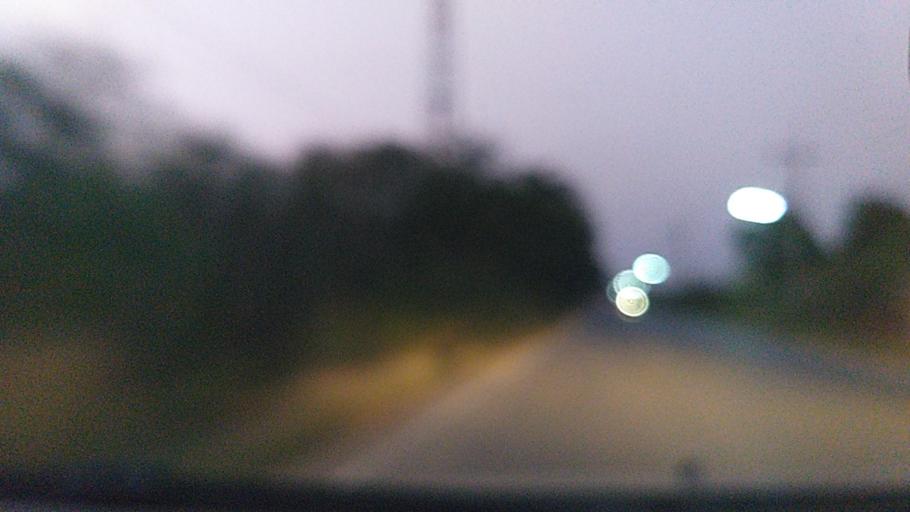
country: TH
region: Sing Buri
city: Sing Buri
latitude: 14.8438
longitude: 100.3924
